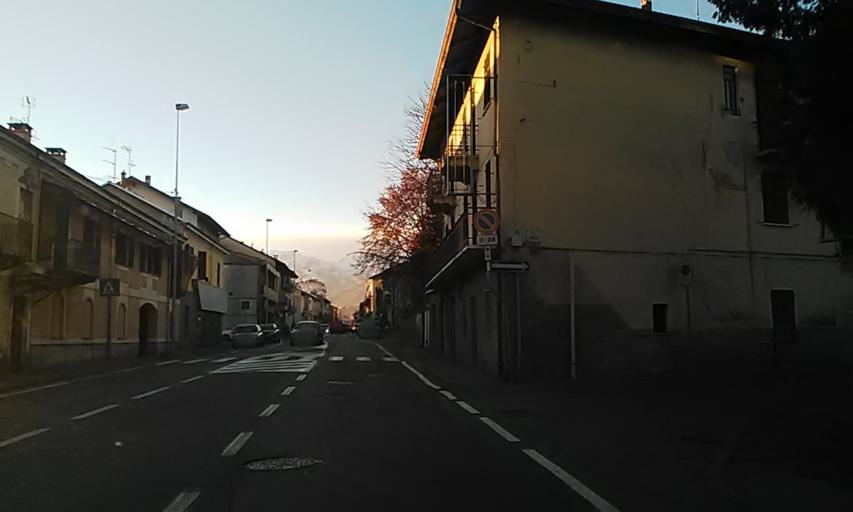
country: IT
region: Piedmont
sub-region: Provincia di Biella
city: Vigliano Biellese
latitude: 45.5640
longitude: 8.1008
